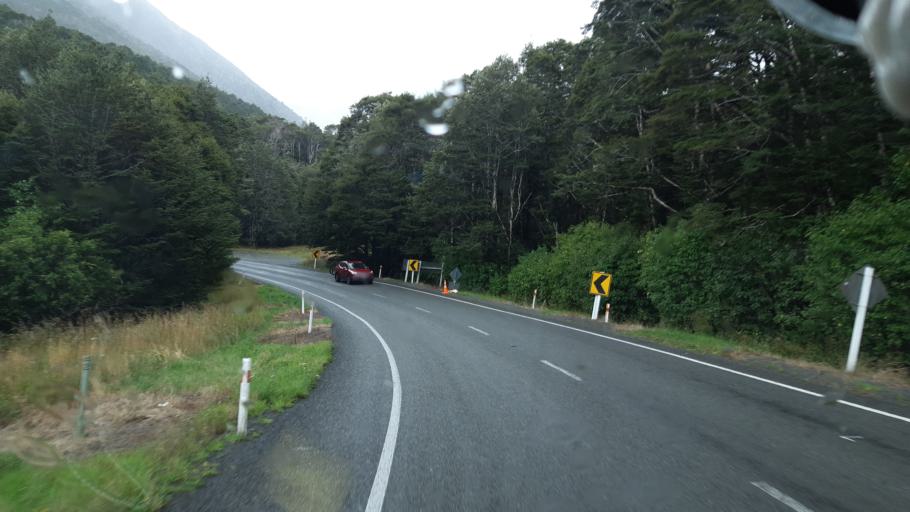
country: NZ
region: Canterbury
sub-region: Hurunui District
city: Amberley
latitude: -42.4457
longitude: 172.4042
